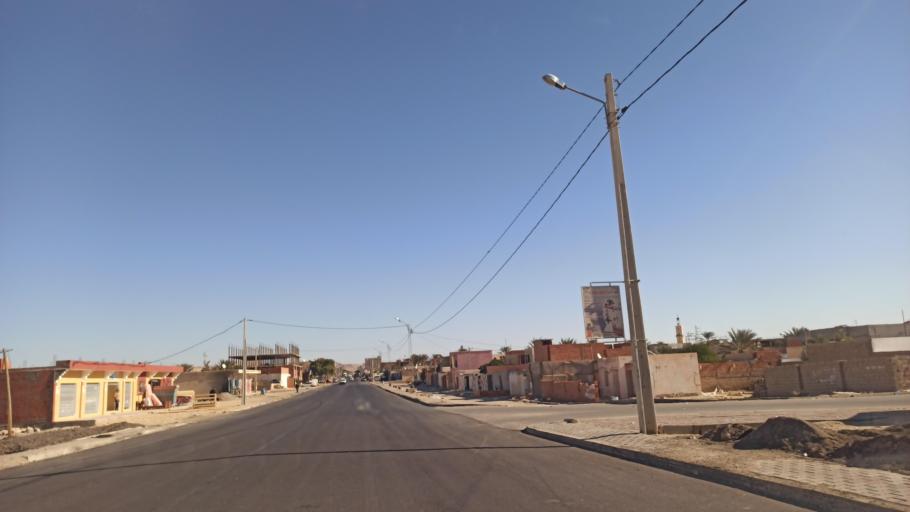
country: TN
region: Gafsa
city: Al Metlaoui
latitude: 34.3108
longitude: 8.3816
